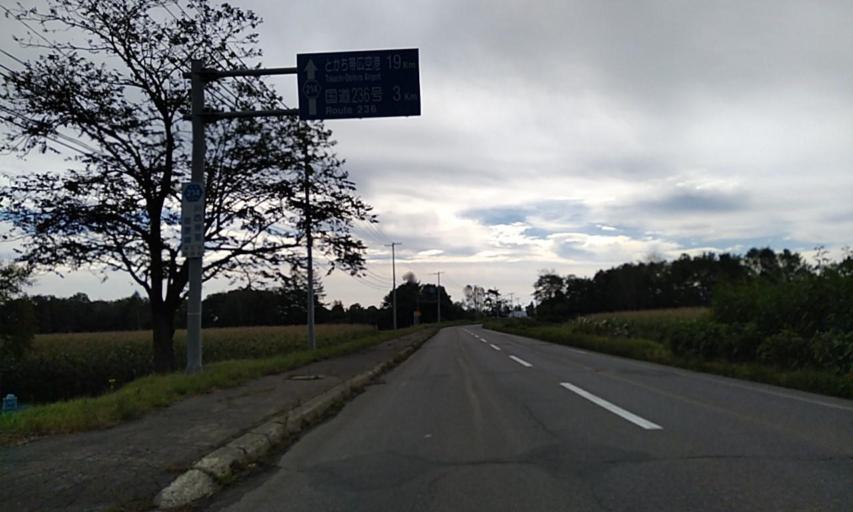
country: JP
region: Hokkaido
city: Obihiro
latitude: 42.8574
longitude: 143.1497
